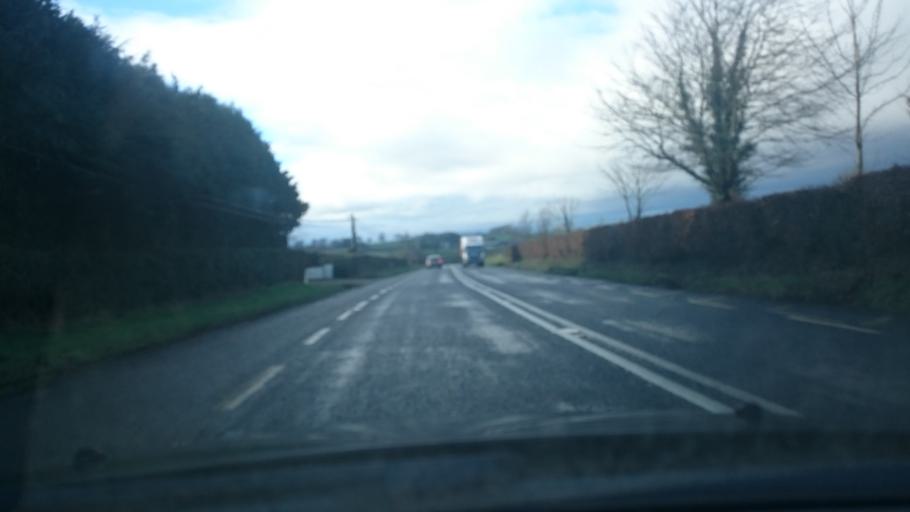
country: IE
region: Leinster
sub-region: Kilkenny
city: Callan
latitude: 52.5661
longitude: -7.3501
